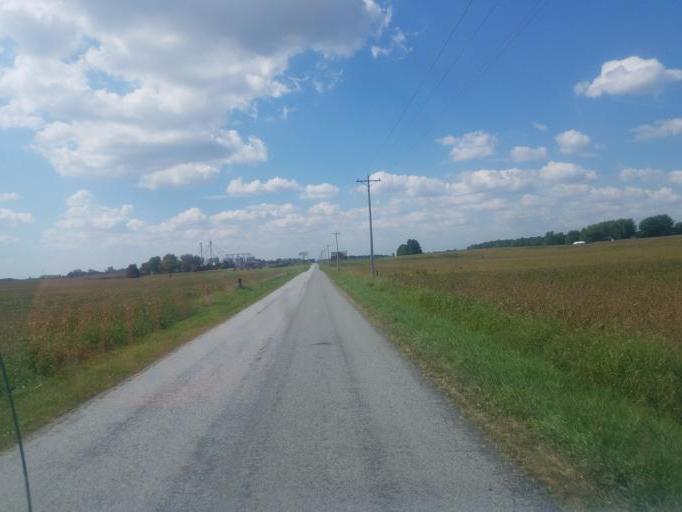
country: US
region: Ohio
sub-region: Hardin County
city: Ada
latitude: 40.6520
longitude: -83.9131
